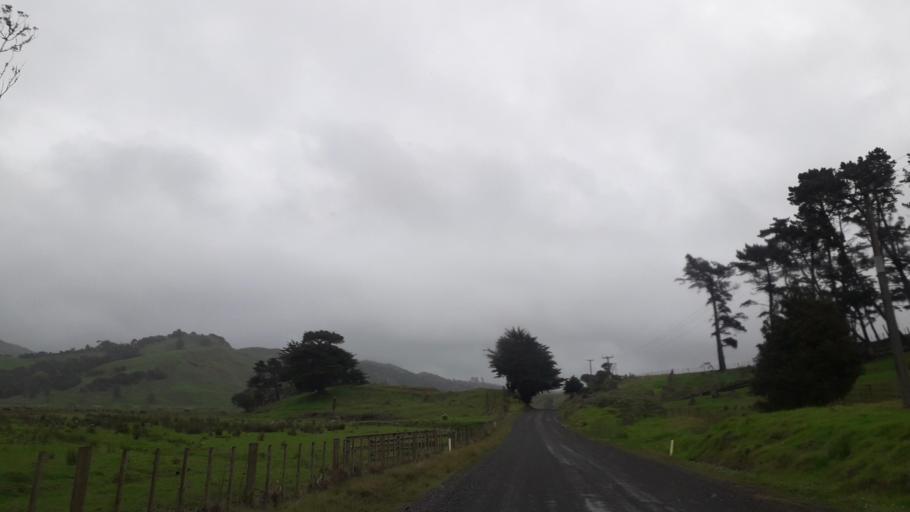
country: NZ
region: Northland
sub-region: Far North District
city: Ahipara
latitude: -35.4179
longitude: 173.3630
